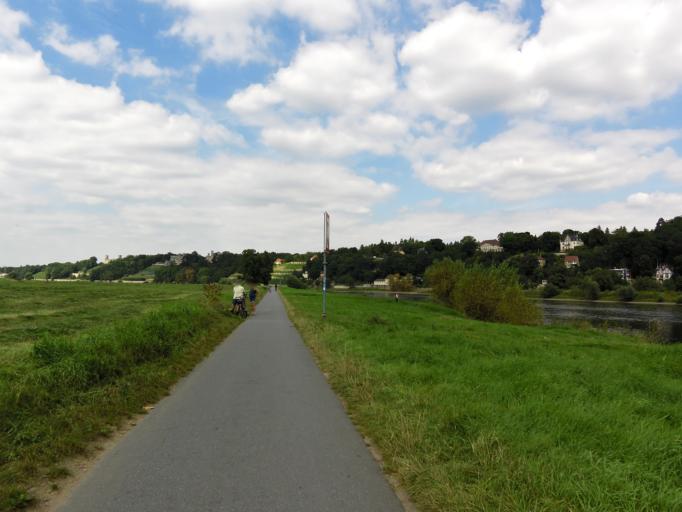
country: DE
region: Saxony
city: Albertstadt
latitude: 51.0546
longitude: 13.8072
